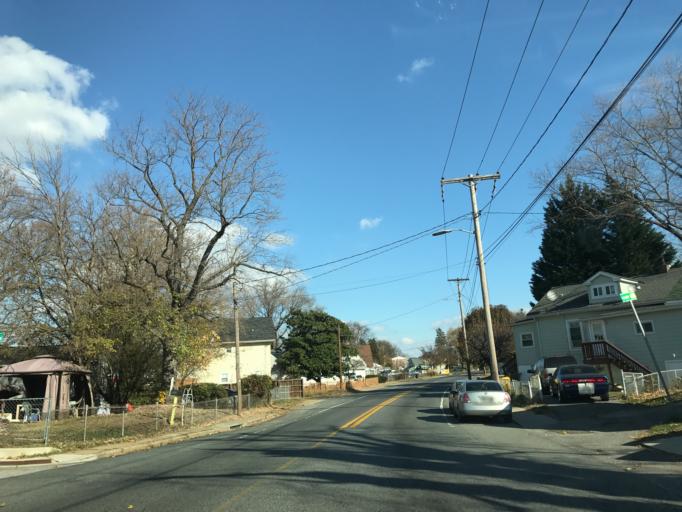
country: US
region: Maryland
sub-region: Anne Arundel County
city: Brooklyn Park
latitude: 39.2316
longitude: -76.6175
